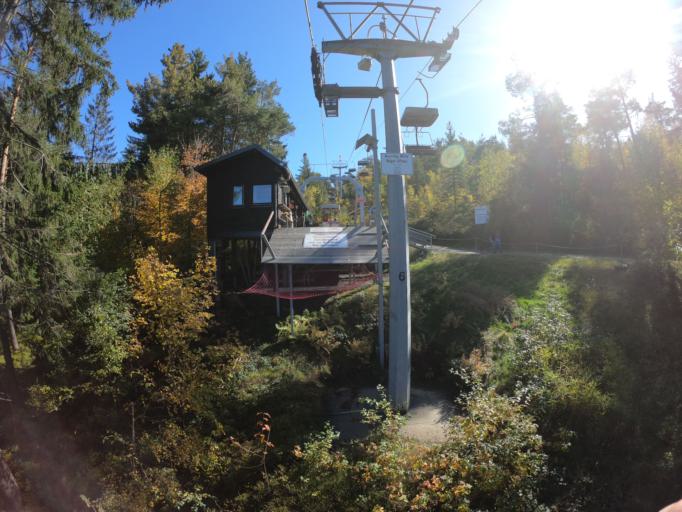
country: DE
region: Bavaria
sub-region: Lower Bavaria
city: Bodenmais
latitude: 49.0594
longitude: 13.1225
